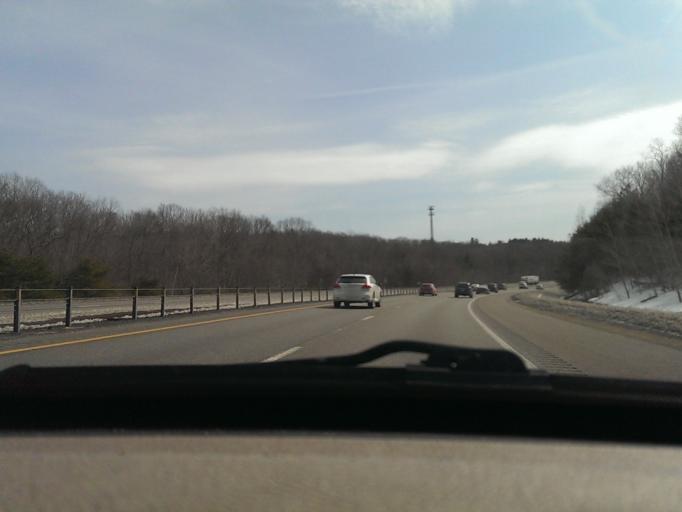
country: US
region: Massachusetts
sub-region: Worcester County
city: Whitinsville
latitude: 42.1345
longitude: -71.7028
